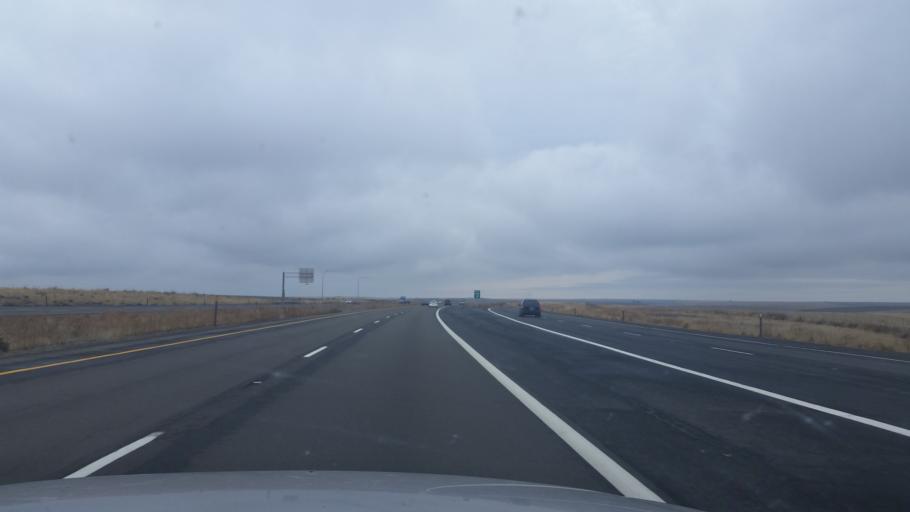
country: US
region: Washington
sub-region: Adams County
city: Ritzville
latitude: 47.1133
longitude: -118.3743
